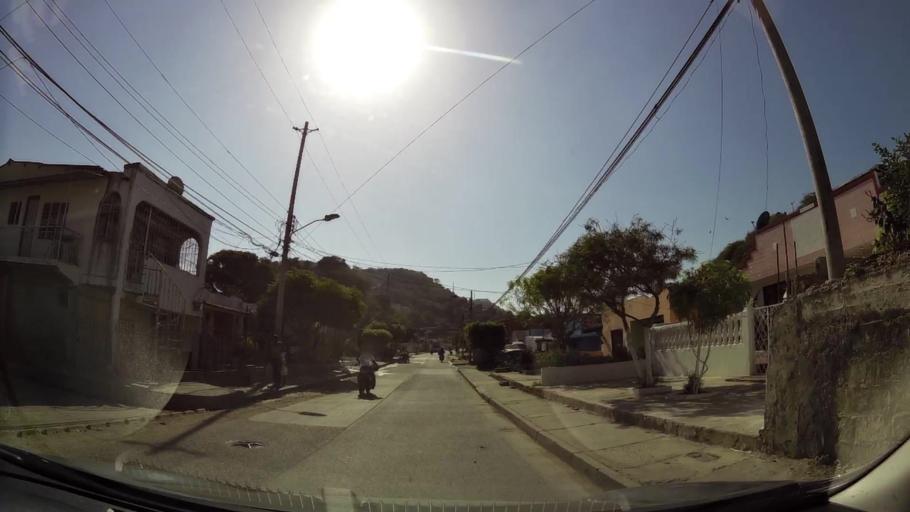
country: CO
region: Bolivar
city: Cartagena
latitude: 10.4284
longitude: -75.5332
